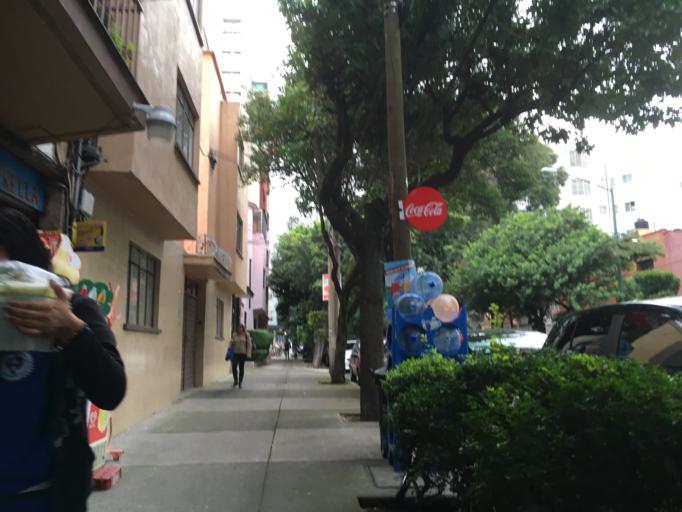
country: MX
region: Mexico City
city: Colonia del Valle
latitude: 19.3800
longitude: -99.1751
